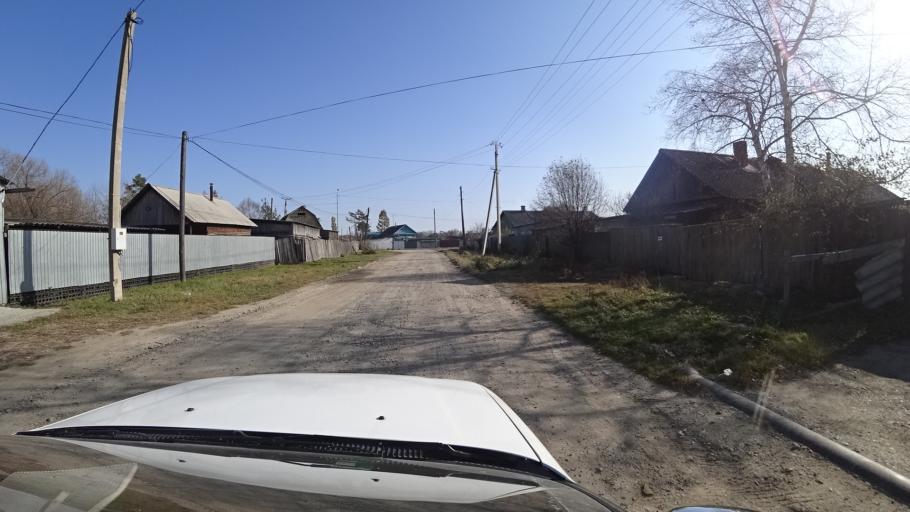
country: RU
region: Primorskiy
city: Dal'nerechensk
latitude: 45.9205
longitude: 133.7226
